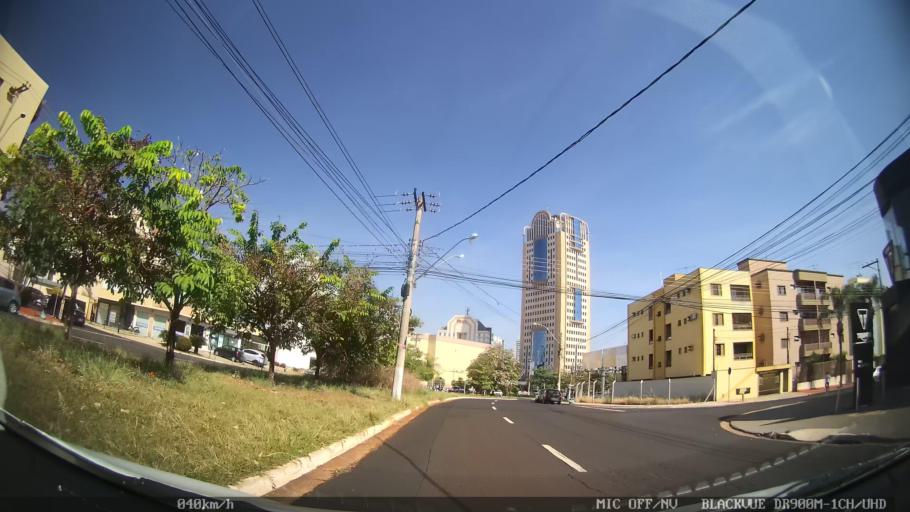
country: BR
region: Sao Paulo
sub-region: Ribeirao Preto
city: Ribeirao Preto
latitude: -21.2101
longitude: -47.8165
